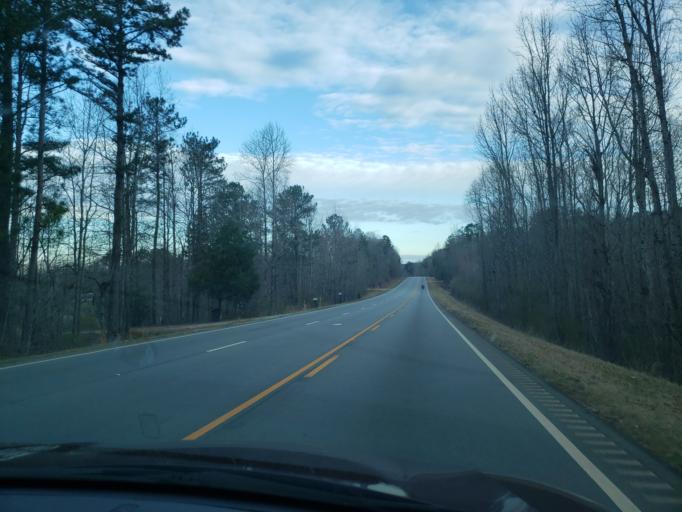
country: US
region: Alabama
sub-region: Randolph County
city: Roanoke
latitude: 33.2145
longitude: -85.4186
